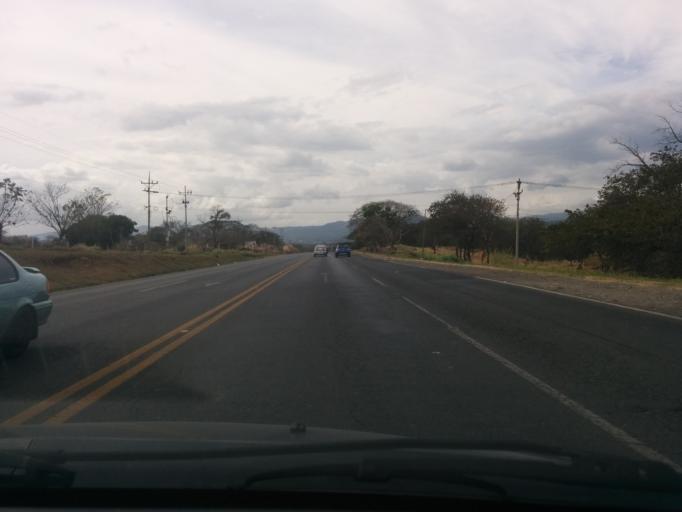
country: CR
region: Alajuela
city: Carrillos
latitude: 10.0000
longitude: -84.2805
